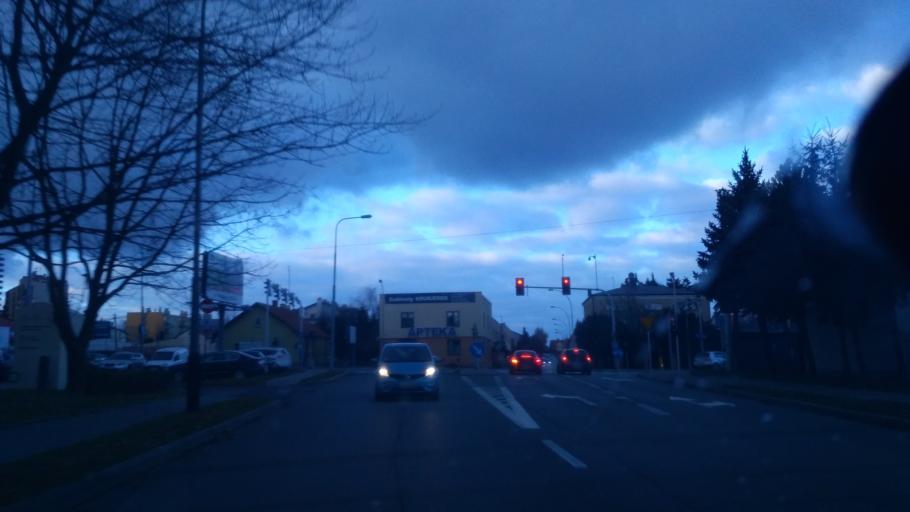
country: PL
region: Subcarpathian Voivodeship
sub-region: Powiat rzeszowski
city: Trzebownisko
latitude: 50.0374
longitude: 22.0400
